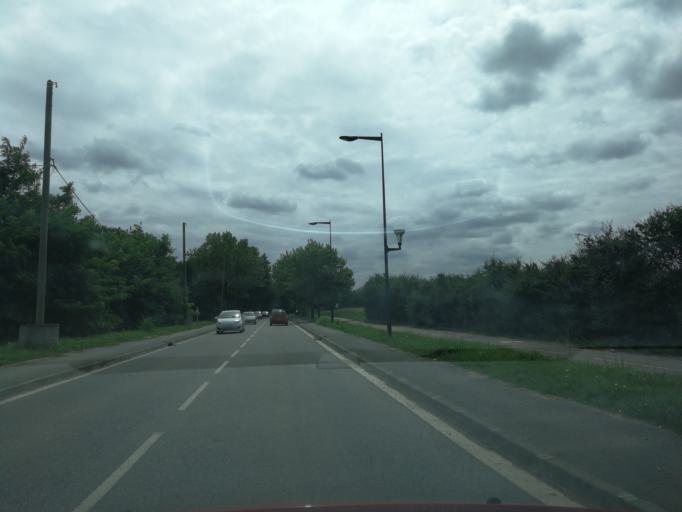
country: FR
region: Midi-Pyrenees
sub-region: Departement de la Haute-Garonne
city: Saint-Orens-de-Gameville
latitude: 43.5765
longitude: 1.5082
